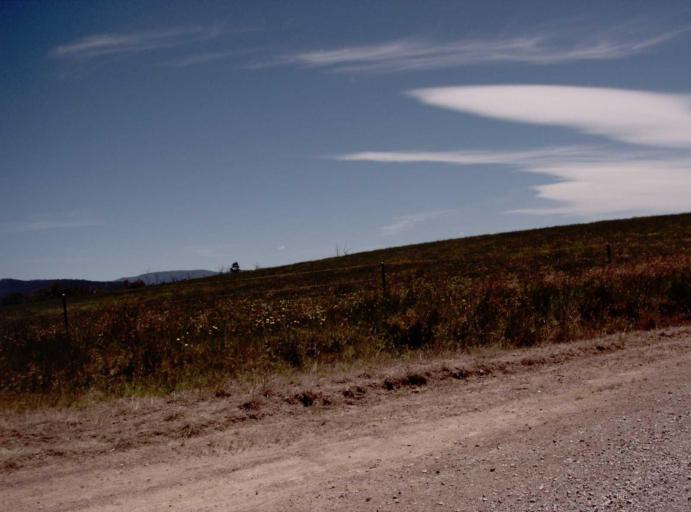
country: AU
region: New South Wales
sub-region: Snowy River
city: Jindabyne
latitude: -37.0932
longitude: 148.2529
